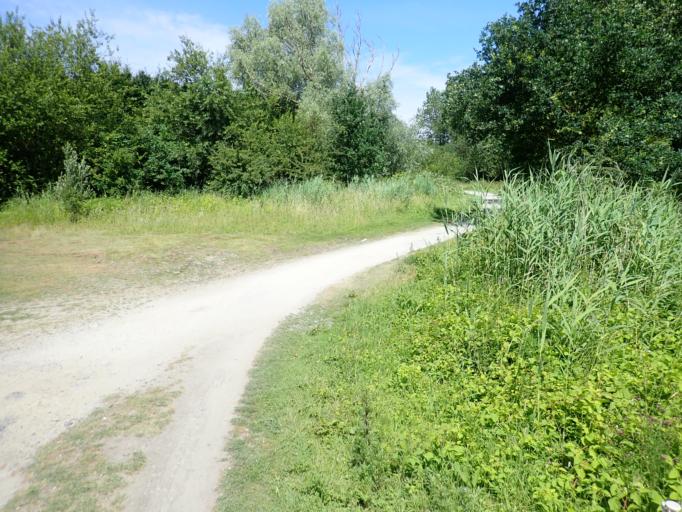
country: BE
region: Flanders
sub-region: Provincie Oost-Vlaanderen
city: Temse
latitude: 51.1212
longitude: 4.2304
